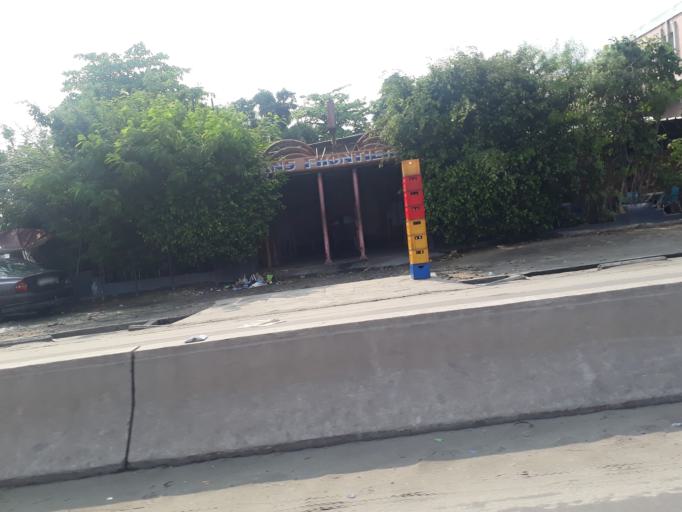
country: CD
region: Kinshasa
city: Kinshasa
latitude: -4.3365
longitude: 15.3055
